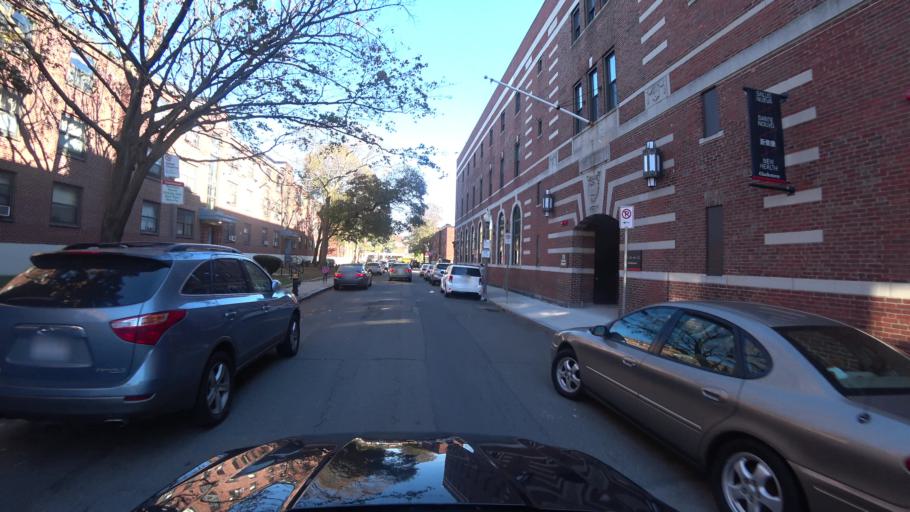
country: US
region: Massachusetts
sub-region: Suffolk County
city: Boston
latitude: 42.3777
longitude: -71.0570
